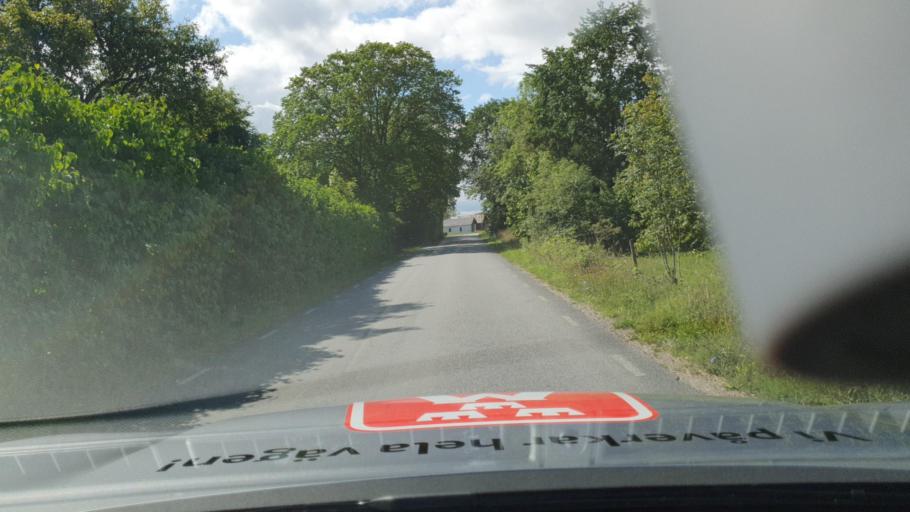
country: SE
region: Gotland
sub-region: Gotland
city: Hemse
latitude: 57.1332
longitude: 18.3496
